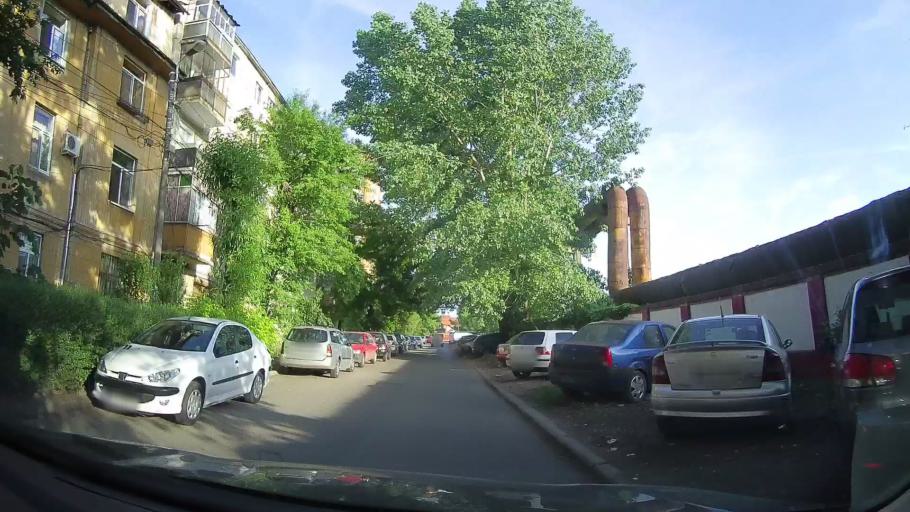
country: RO
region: Timis
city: Timisoara
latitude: 45.7480
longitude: 21.2458
